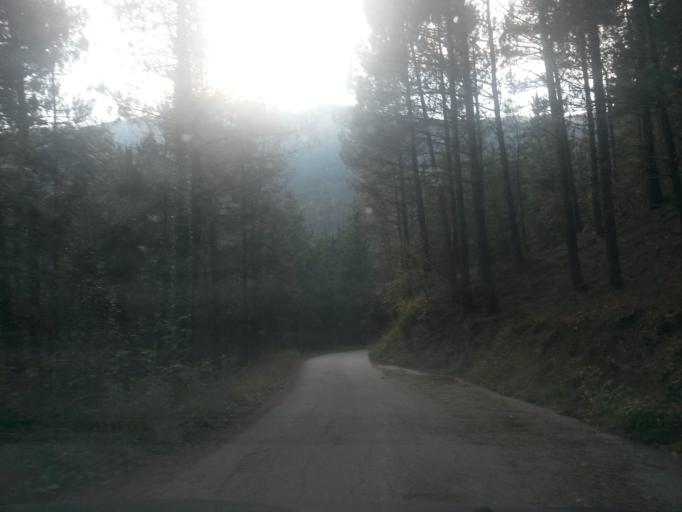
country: ES
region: Catalonia
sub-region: Provincia de Girona
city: Susqueda
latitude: 41.9490
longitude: 2.5528
